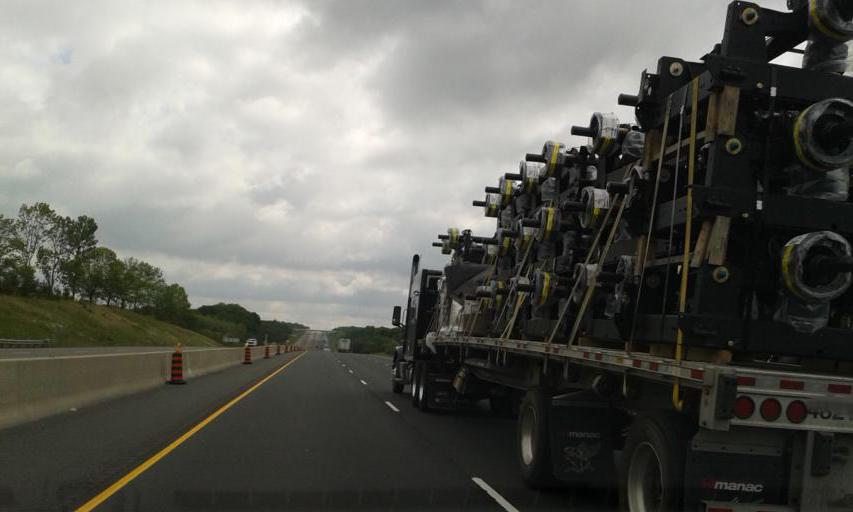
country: CA
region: Ontario
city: Cobourg
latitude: 43.9362
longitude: -78.4659
